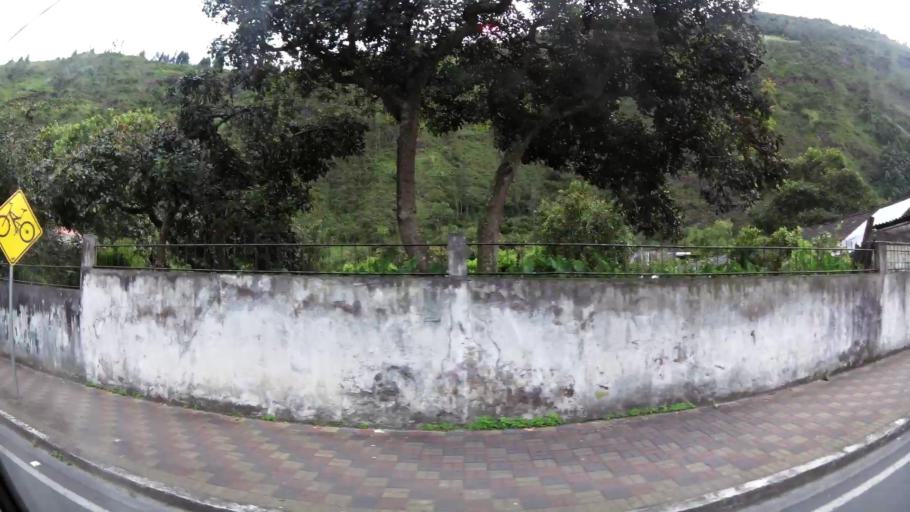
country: EC
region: Tungurahua
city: Banos
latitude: -1.3956
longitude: -78.4058
